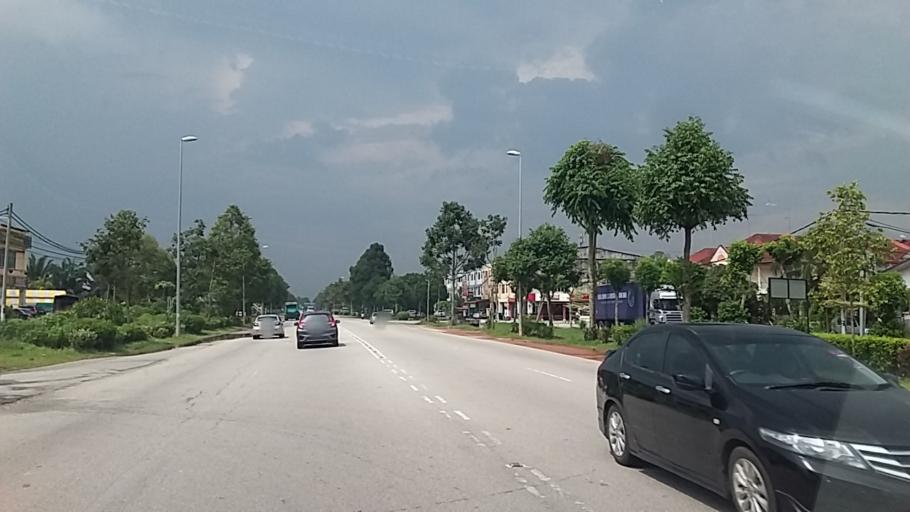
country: MY
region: Johor
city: Parit Raja
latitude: 1.8677
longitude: 103.1197
